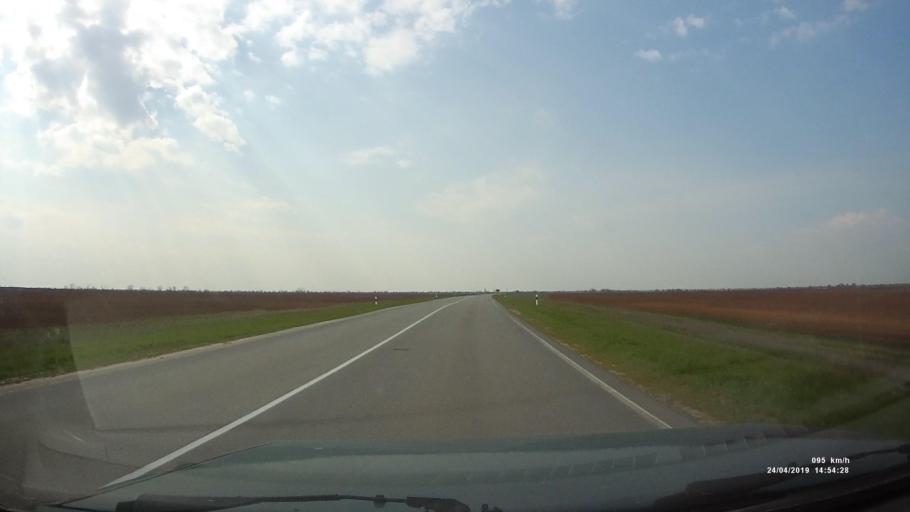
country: RU
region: Rostov
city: Remontnoye
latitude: 46.5346
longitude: 43.6382
